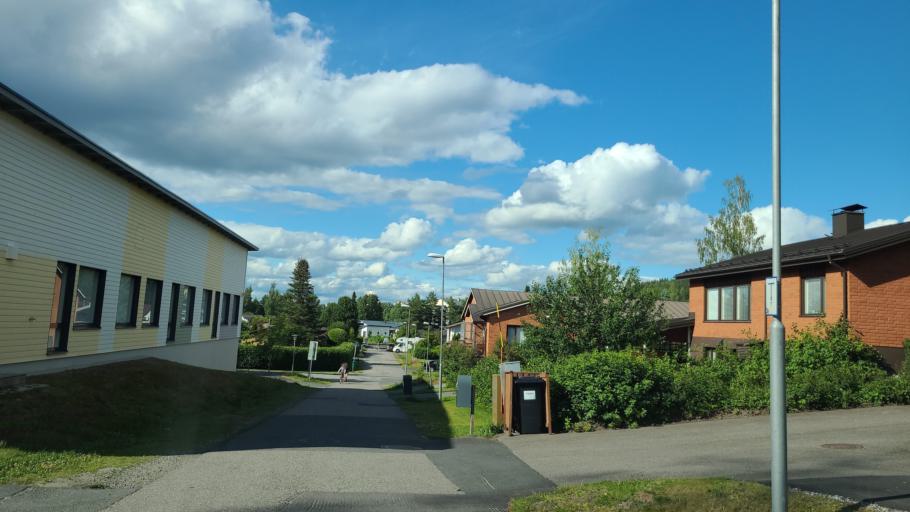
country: FI
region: Northern Savo
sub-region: Kuopio
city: Kuopio
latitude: 62.9252
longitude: 27.6283
